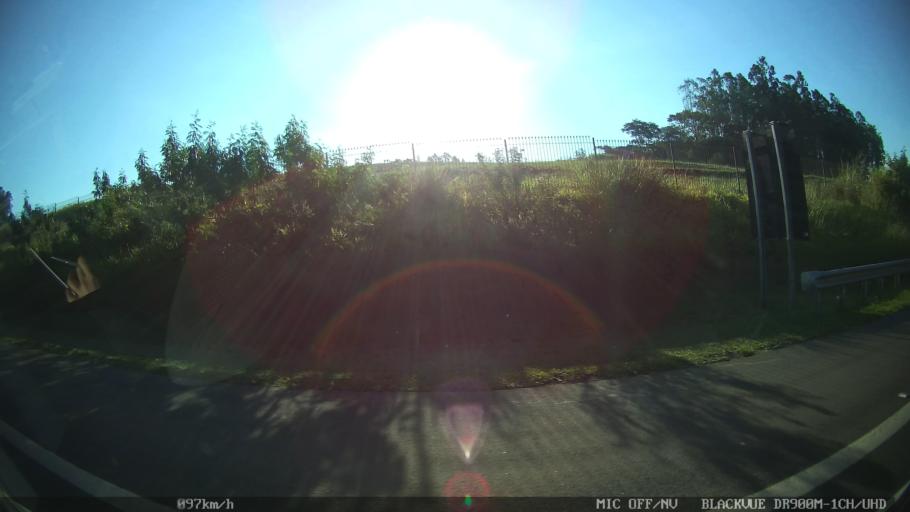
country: BR
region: Sao Paulo
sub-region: Piracicaba
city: Piracicaba
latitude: -22.6976
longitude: -47.6384
